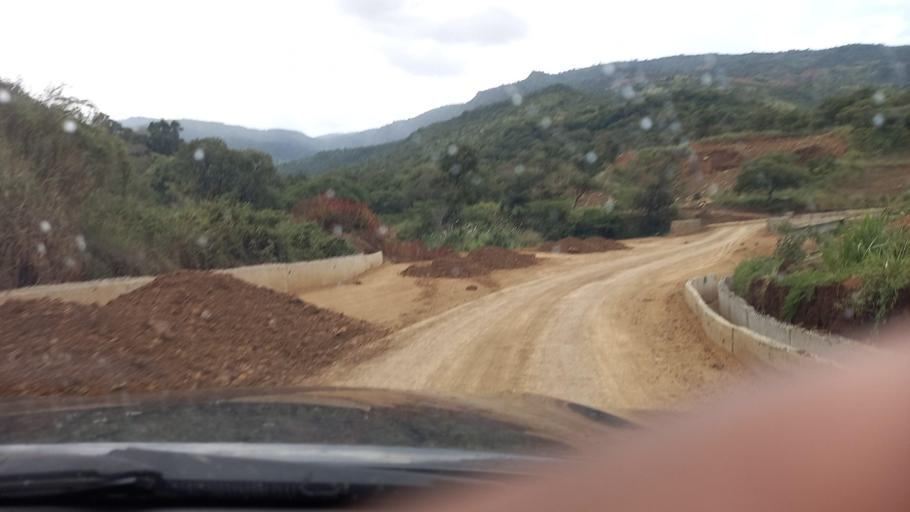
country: ET
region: Southern Nations, Nationalities, and People's Region
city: Mizan Teferi
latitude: 6.1886
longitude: 35.6747
